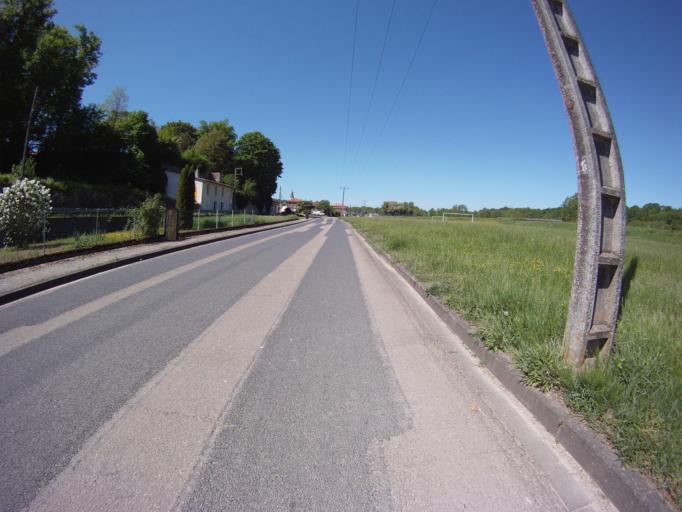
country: FR
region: Lorraine
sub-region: Departement de Meurthe-et-Moselle
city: Dommartin-les-Toul
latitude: 48.6435
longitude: 5.9361
